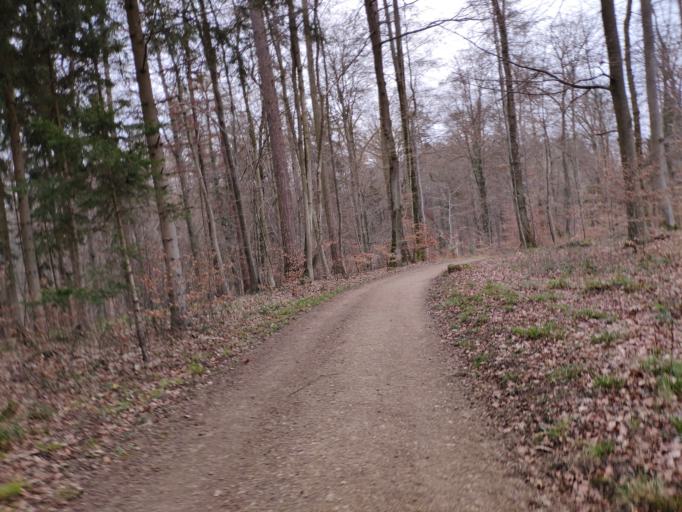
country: DE
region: Baden-Wuerttemberg
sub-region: Freiburg Region
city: Inzlingen
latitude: 47.5978
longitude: 7.6875
